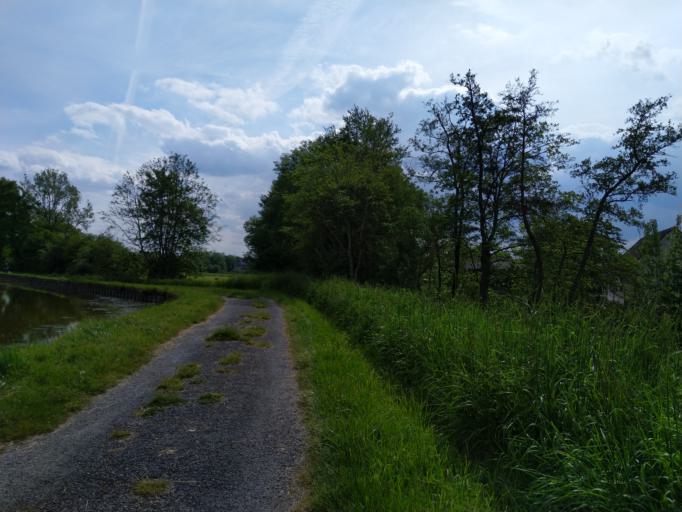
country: FR
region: Picardie
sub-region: Departement de l'Aisne
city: Guise
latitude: 49.9305
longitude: 3.5868
